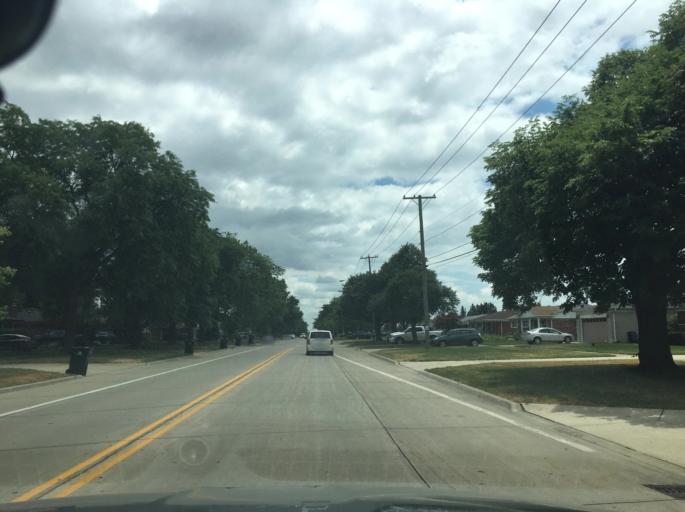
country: US
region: Michigan
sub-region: Macomb County
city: Fraser
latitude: 42.5220
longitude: -82.9690
